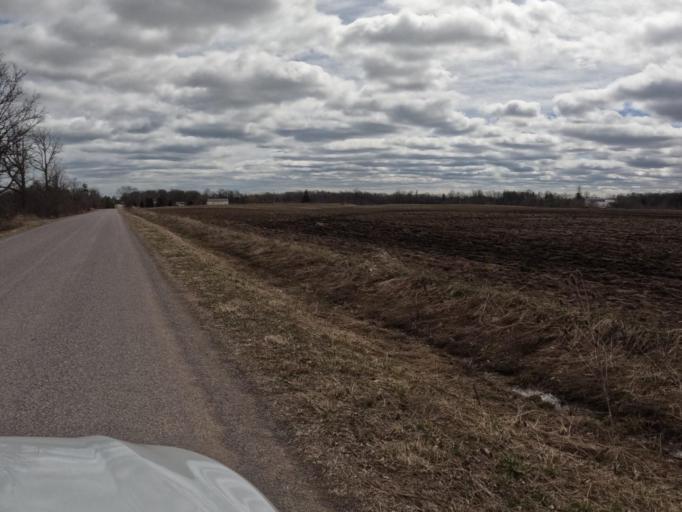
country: CA
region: Ontario
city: Norfolk County
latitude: 42.8584
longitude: -80.1731
